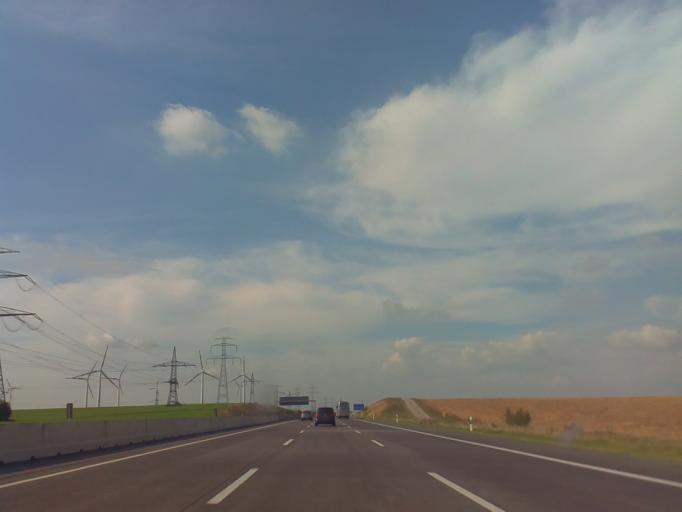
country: DE
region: Thuringia
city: Bischofroda
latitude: 51.0023
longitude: 10.4038
